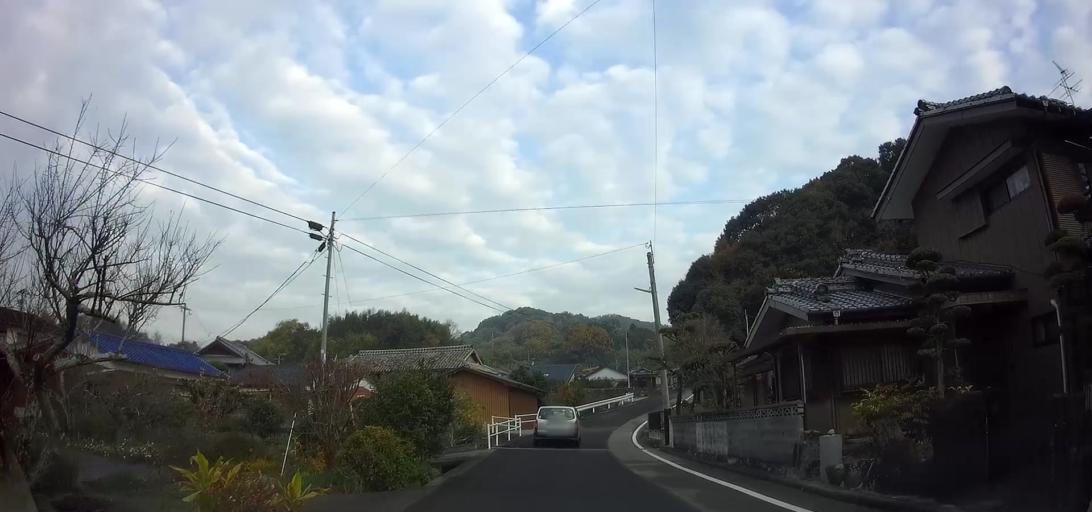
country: JP
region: Nagasaki
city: Shimabara
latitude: 32.6564
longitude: 130.2497
